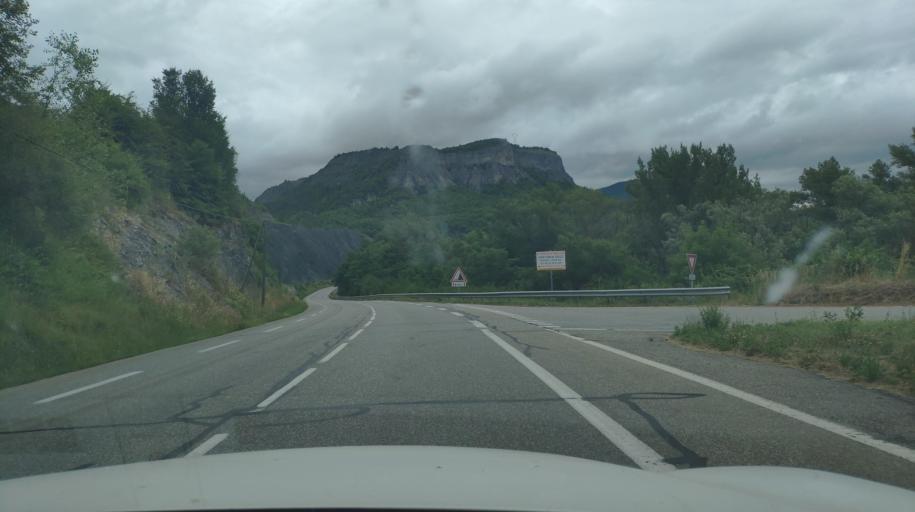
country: FR
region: Provence-Alpes-Cote d'Azur
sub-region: Departement des Hautes-Alpes
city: Tallard
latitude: 44.4744
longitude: 6.0771
